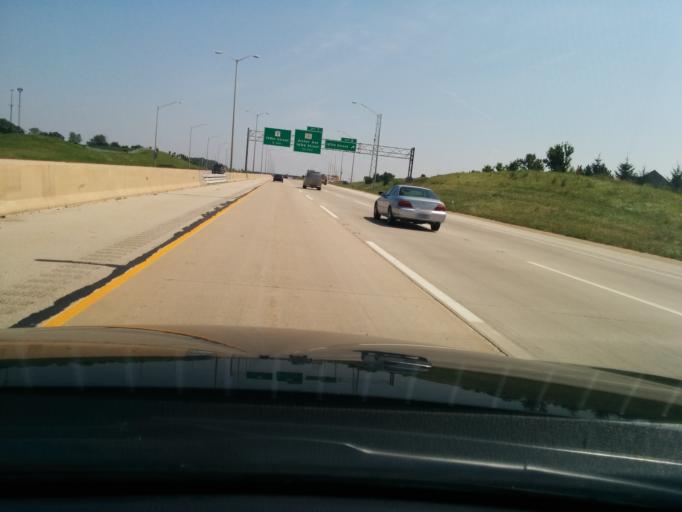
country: US
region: Illinois
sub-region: Cook County
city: Lemont
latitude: 41.6632
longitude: -88.0241
